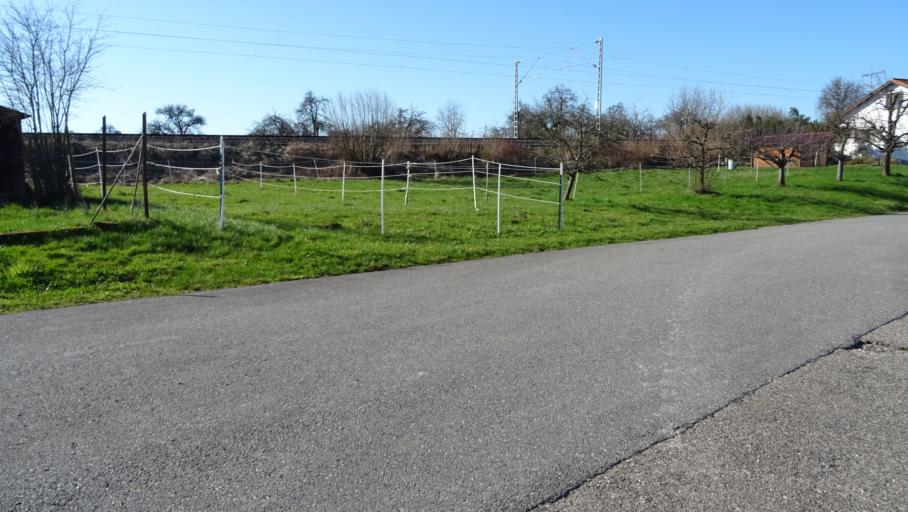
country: DE
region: Baden-Wuerttemberg
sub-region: Karlsruhe Region
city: Seckach
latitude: 49.4271
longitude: 9.2876
